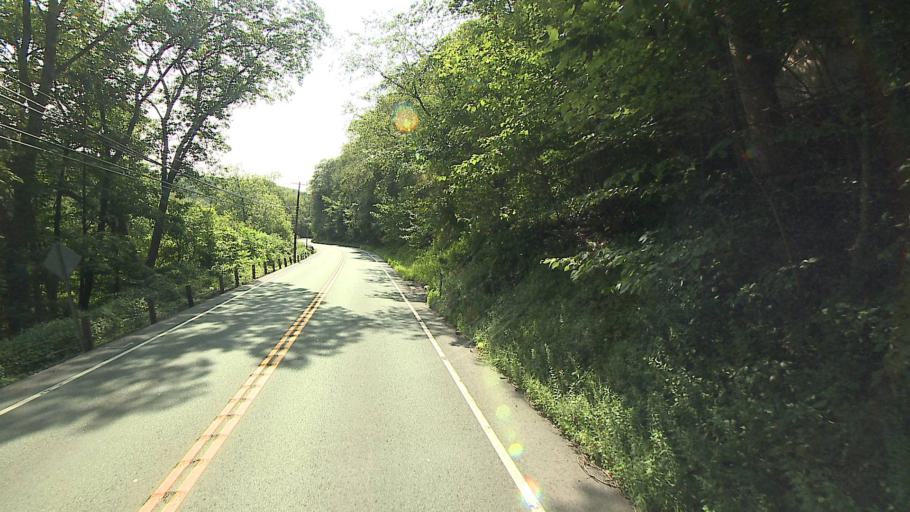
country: US
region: Connecticut
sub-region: Fairfield County
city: Sherman
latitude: 41.6326
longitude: -73.4731
